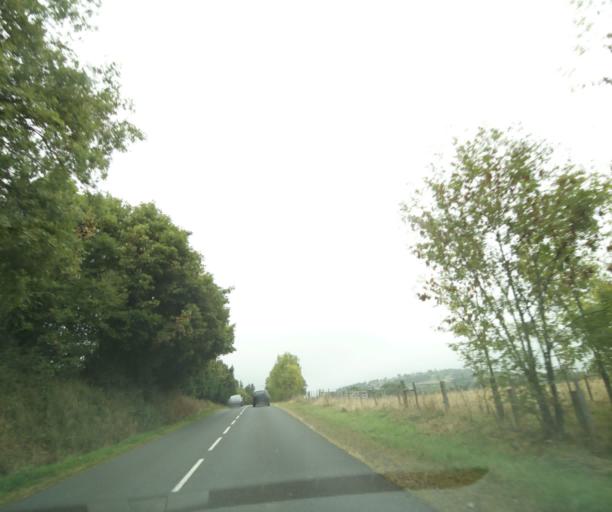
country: FR
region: Auvergne
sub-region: Departement du Puy-de-Dome
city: Saint-Genes-Champanelle
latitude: 45.7149
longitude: 3.0181
